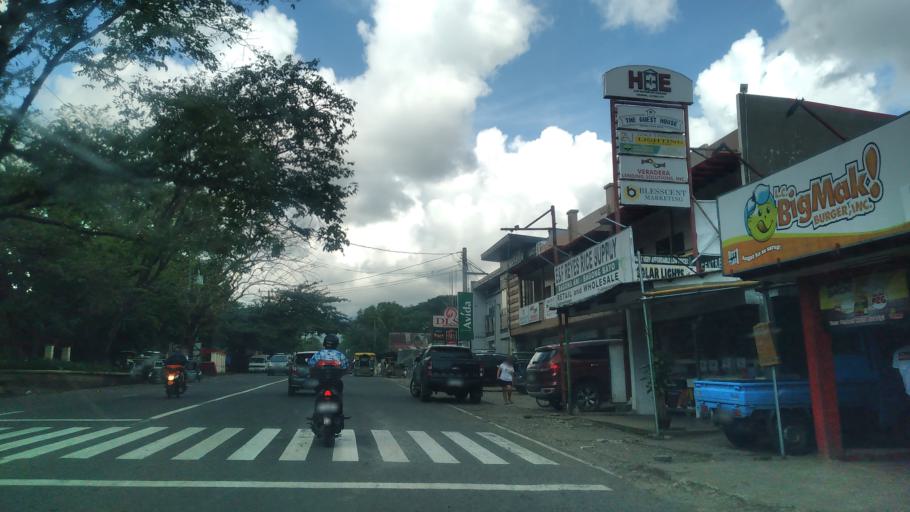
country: PH
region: Calabarzon
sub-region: Province of Quezon
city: Isabang
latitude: 13.9553
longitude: 121.5725
